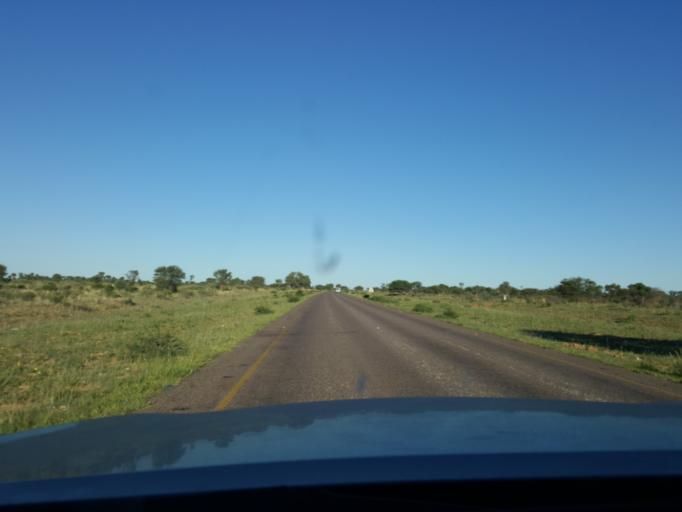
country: BW
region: Southern
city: Khakhea
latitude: -24.3045
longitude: 23.4008
